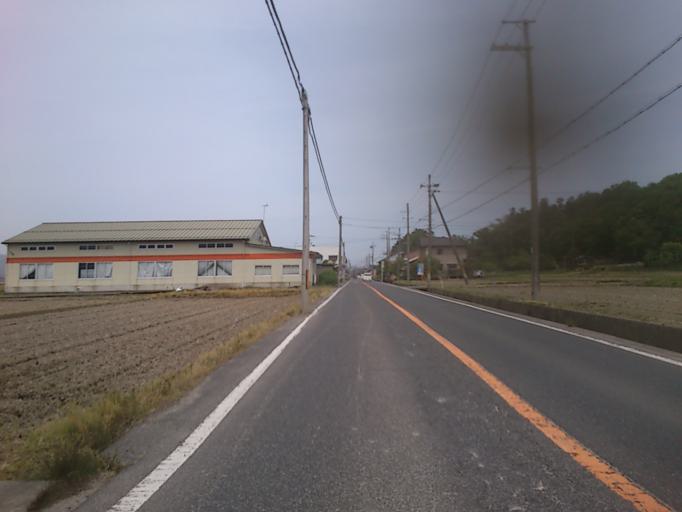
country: JP
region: Kyoto
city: Miyazu
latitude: 35.5930
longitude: 135.0983
